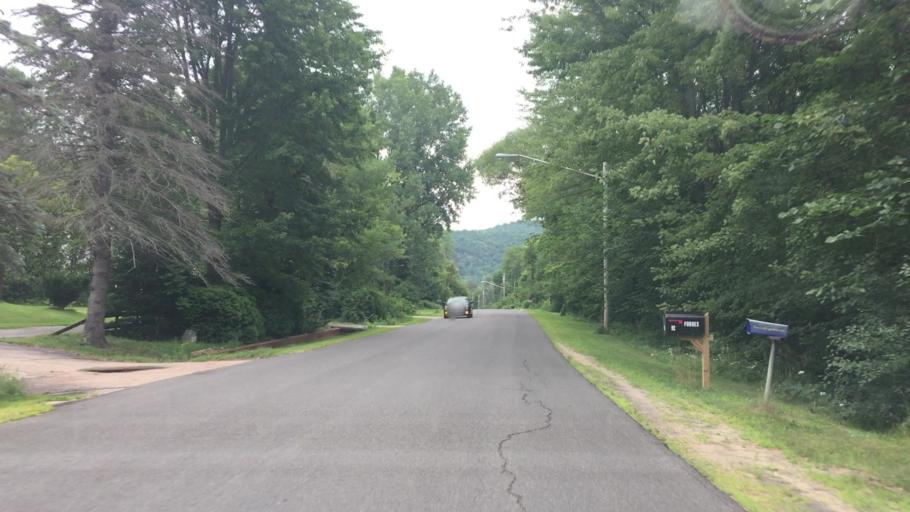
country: US
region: New York
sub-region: Essex County
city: Keeseville
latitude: 44.4655
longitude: -73.5796
